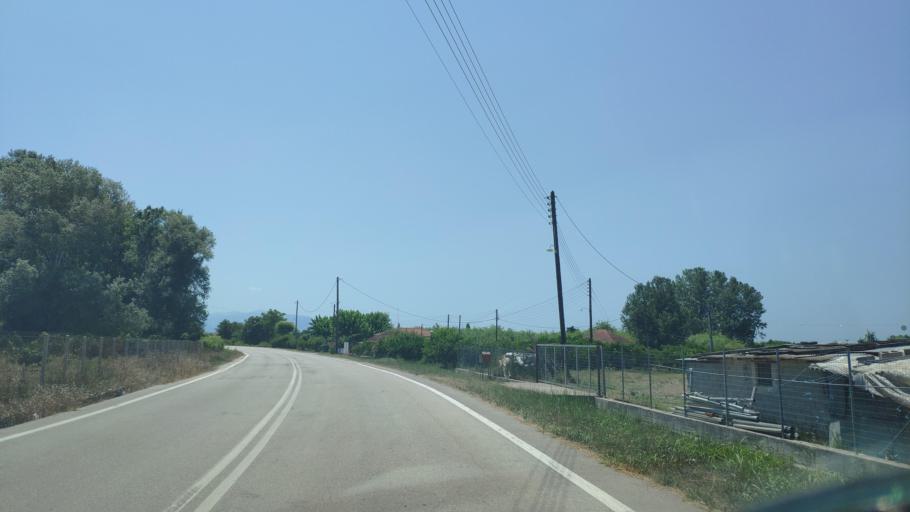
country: GR
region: Epirus
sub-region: Nomos Artas
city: Neochori
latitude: 39.0894
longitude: 21.0151
